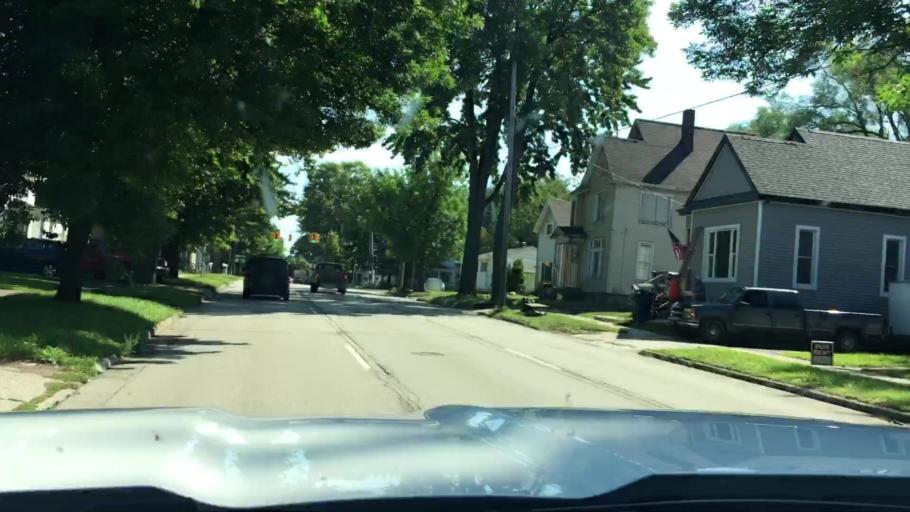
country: US
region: Michigan
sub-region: Bay County
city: Bay City
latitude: 43.5975
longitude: -83.9066
